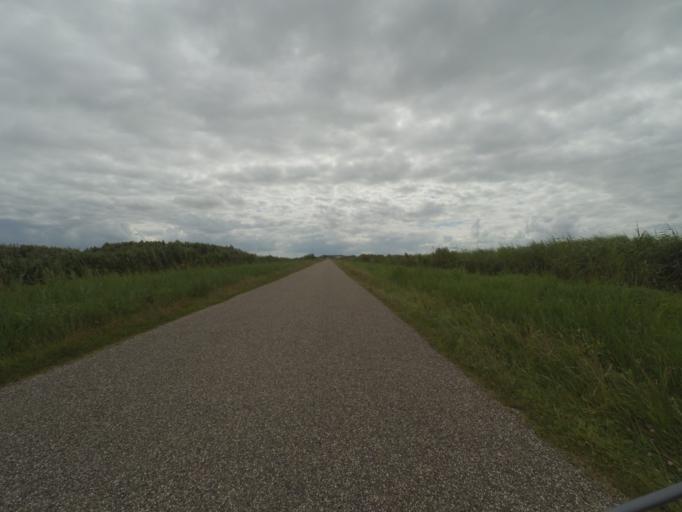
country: NL
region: Friesland
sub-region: Gemeente Dongeradeel
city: Anjum
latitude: 53.3501
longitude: 6.1530
